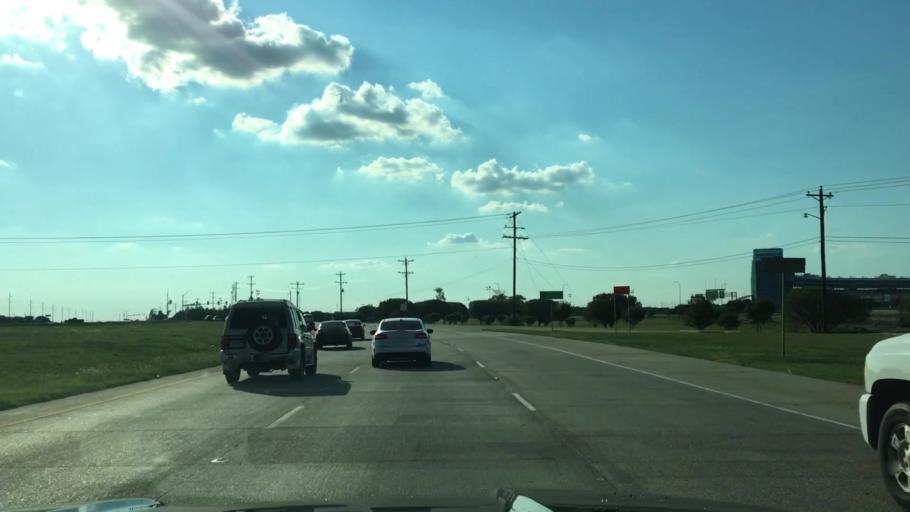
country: US
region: Texas
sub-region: Denton County
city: Roanoke
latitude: 33.0268
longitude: -97.2752
